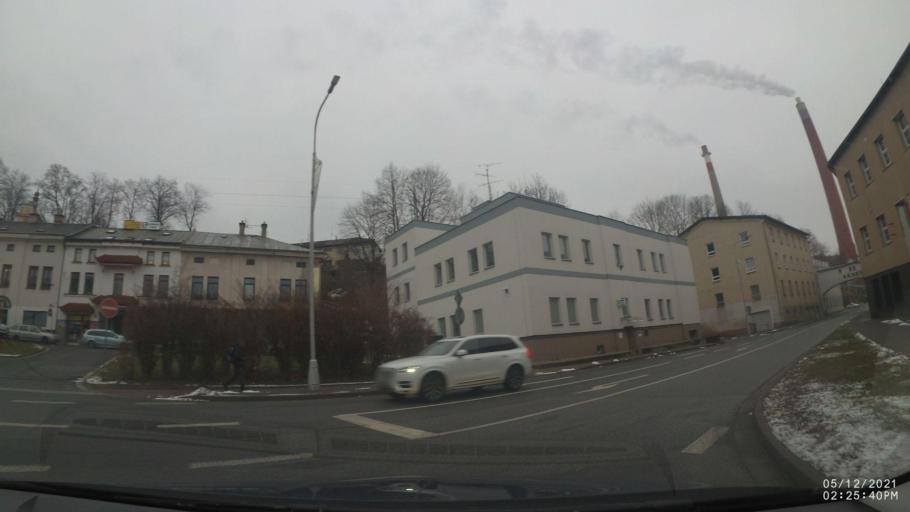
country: CZ
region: Kralovehradecky
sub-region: Okres Nachod
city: Nachod
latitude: 50.4213
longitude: 16.1676
